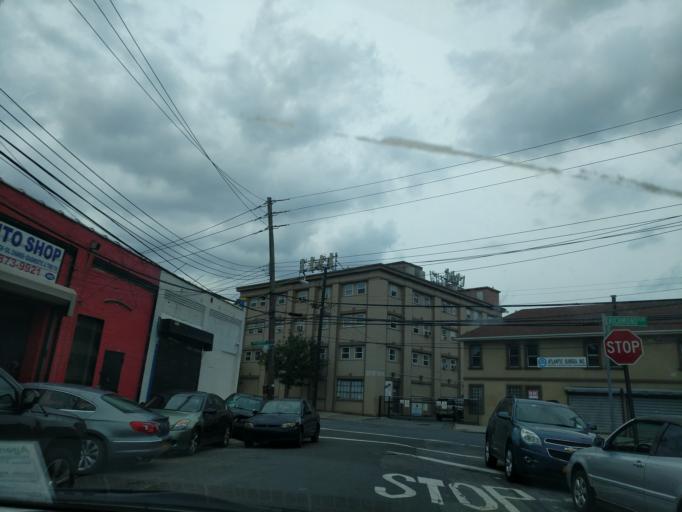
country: US
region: New York
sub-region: Richmond County
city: Bloomfield
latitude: 40.6378
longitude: -74.1624
